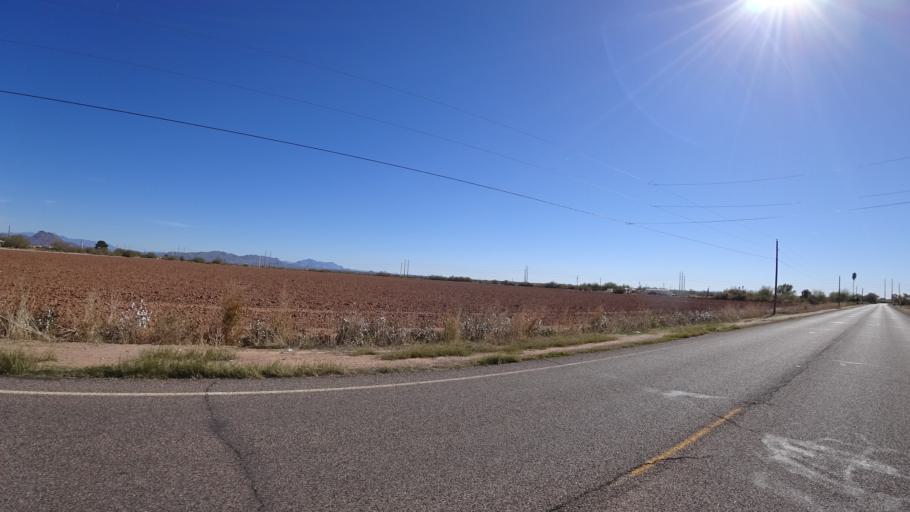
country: US
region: Arizona
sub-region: Maricopa County
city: Mesa
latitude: 33.4907
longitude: -111.8222
